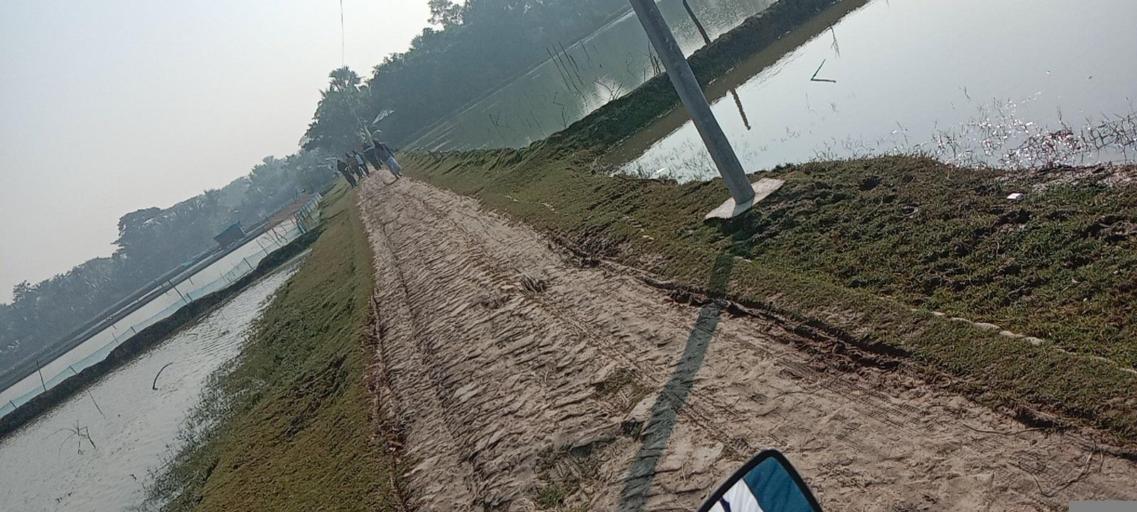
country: BD
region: Khulna
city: Phultala
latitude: 22.6097
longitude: 89.5864
